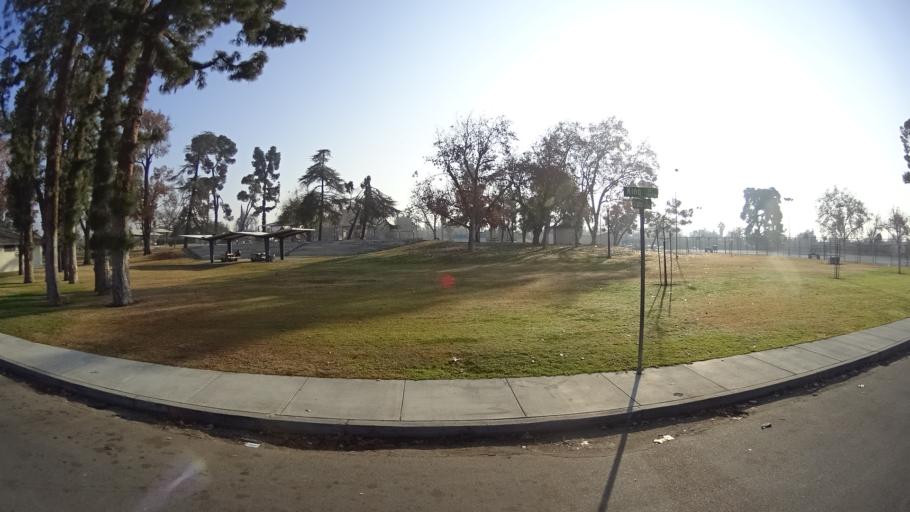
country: US
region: California
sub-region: Kern County
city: Bakersfield
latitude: 35.3889
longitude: -118.9869
